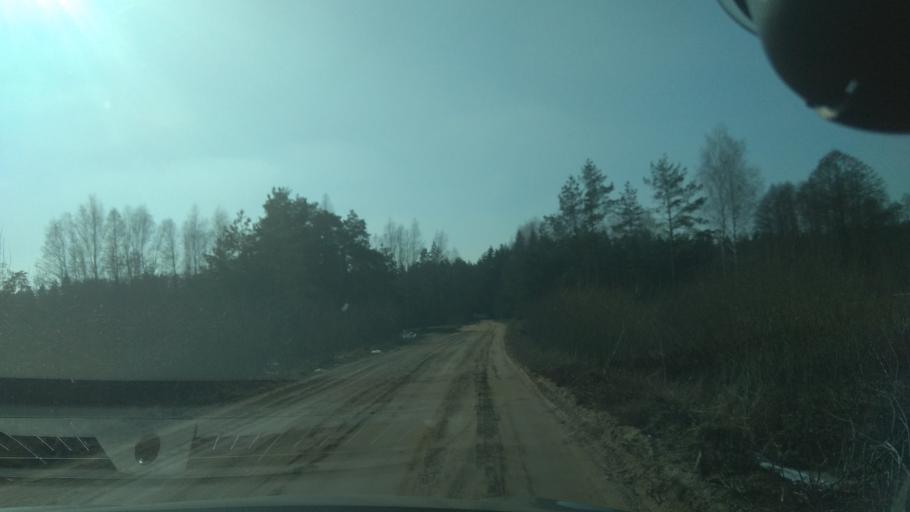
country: LT
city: Baltoji Voke
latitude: 54.4831
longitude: 25.2624
